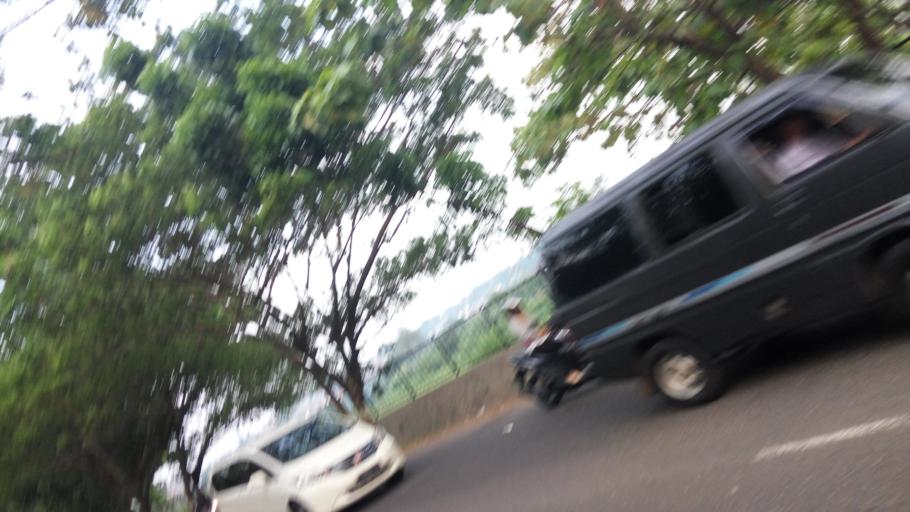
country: ID
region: Central Java
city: Semarang
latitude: -7.0029
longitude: 110.3957
